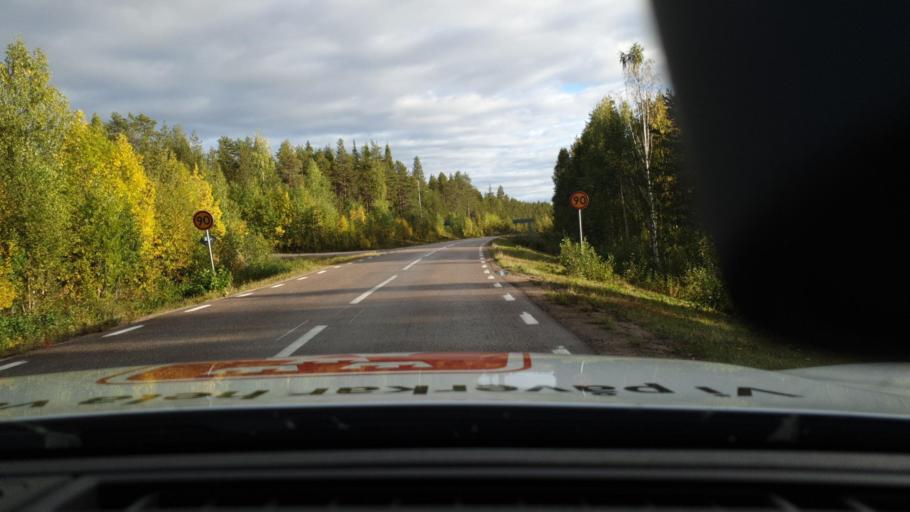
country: SE
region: Norrbotten
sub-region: Overkalix Kommun
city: OEverkalix
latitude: 66.6507
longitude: 22.7182
